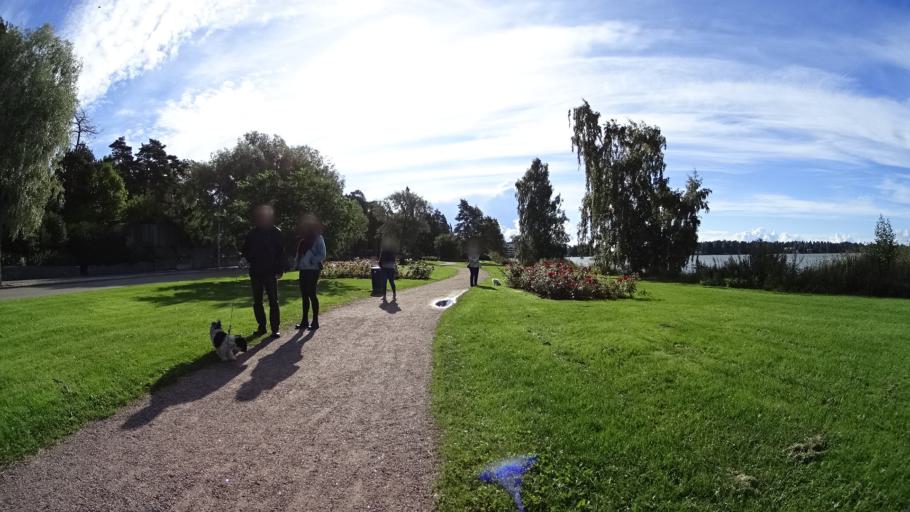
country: FI
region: Uusimaa
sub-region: Helsinki
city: Teekkarikylae
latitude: 60.1971
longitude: 24.8679
